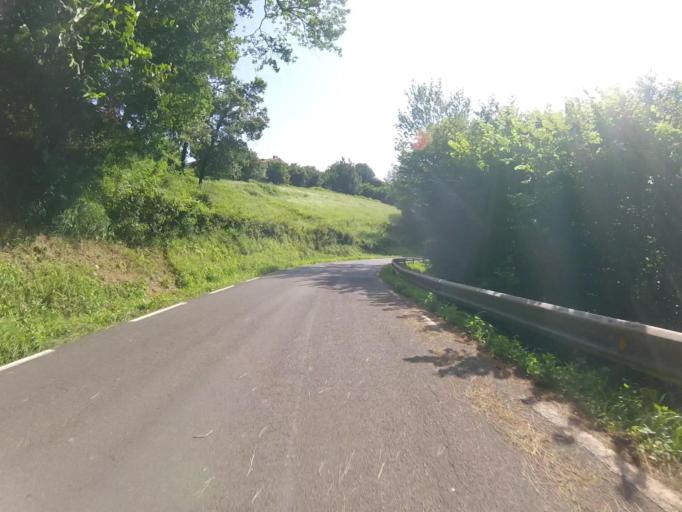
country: ES
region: Basque Country
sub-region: Provincia de Guipuzcoa
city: Alquiza
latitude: 43.1710
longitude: -2.1116
